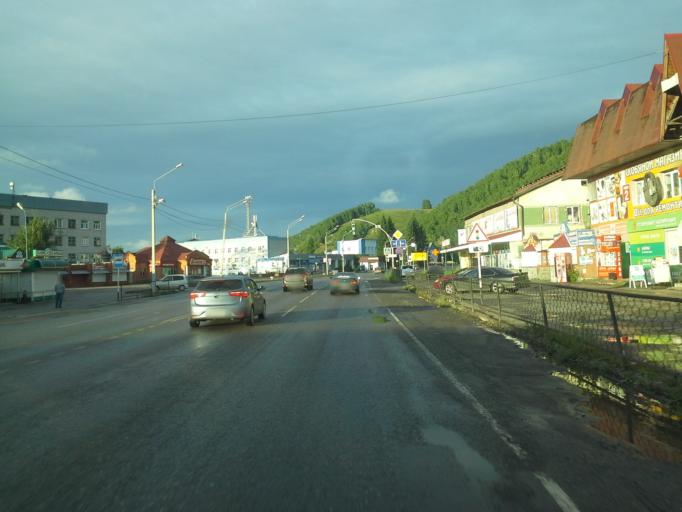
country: RU
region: Khabarovsk Krai
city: Mayma
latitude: 52.0037
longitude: 85.9003
